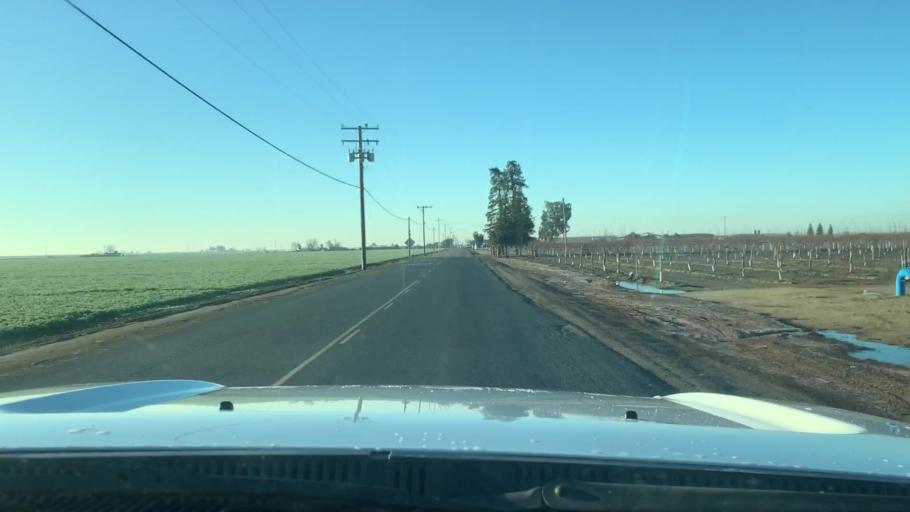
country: US
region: California
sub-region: Kings County
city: Corcoran
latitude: 36.2102
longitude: -119.4930
